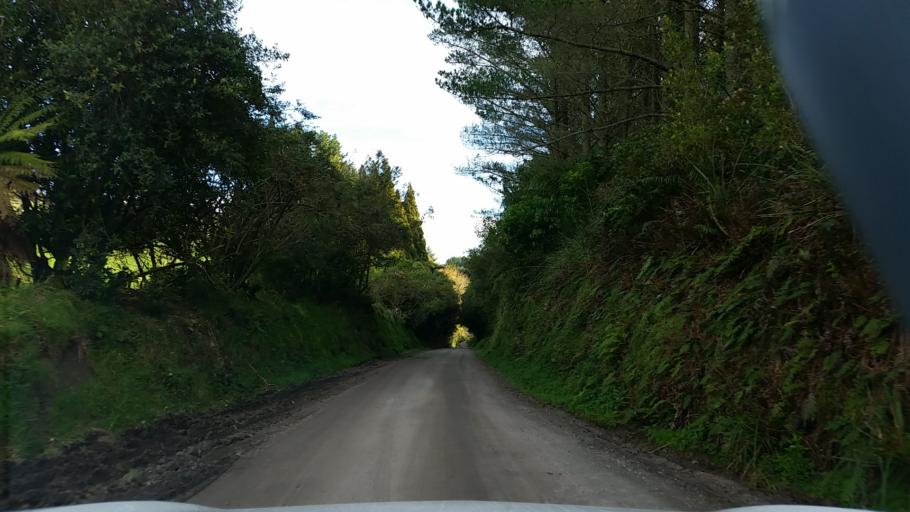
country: NZ
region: Bay of Plenty
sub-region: Rotorua District
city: Rotorua
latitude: -38.2385
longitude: 176.3592
